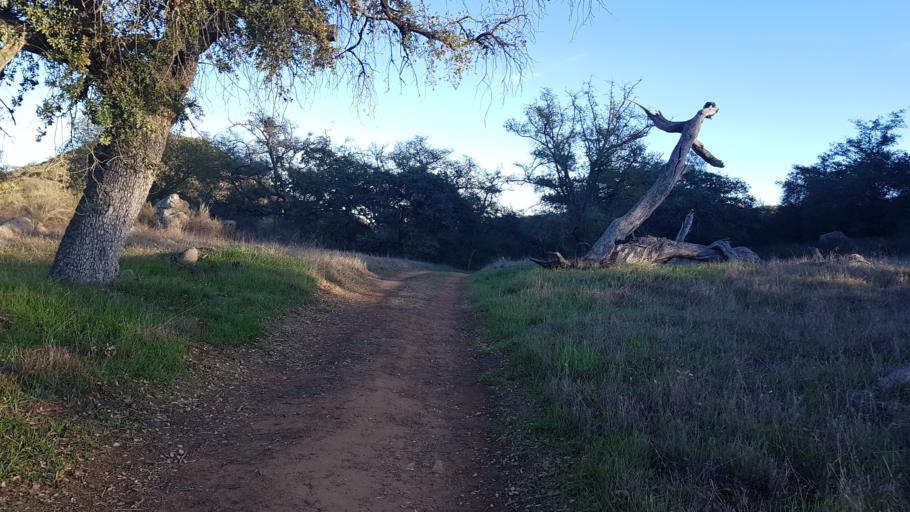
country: US
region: California
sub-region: San Diego County
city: Valley Center
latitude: 33.2073
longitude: -117.0643
